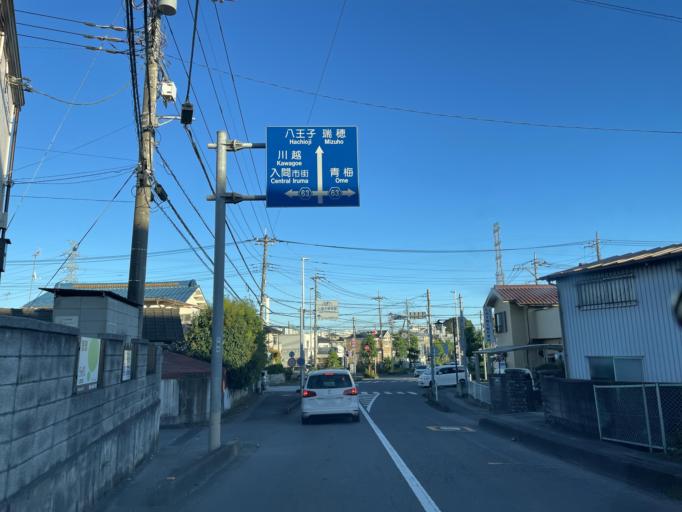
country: JP
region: Saitama
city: Hanno
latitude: 35.8239
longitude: 139.3633
